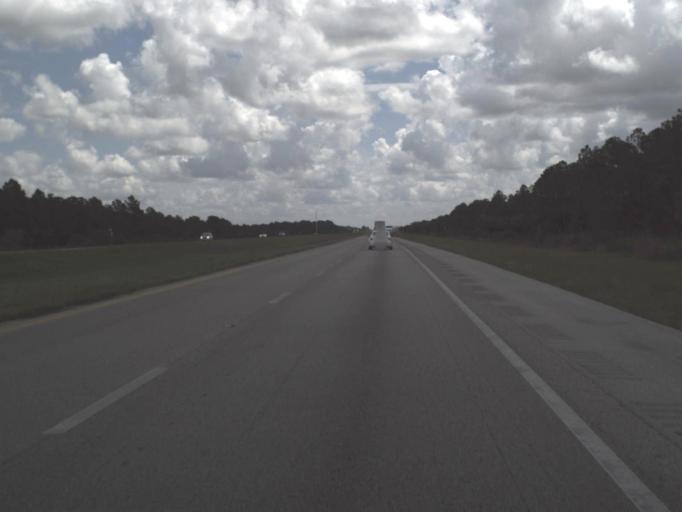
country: US
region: Florida
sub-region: Collier County
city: Golden Gate
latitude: 26.1529
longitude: -81.5718
